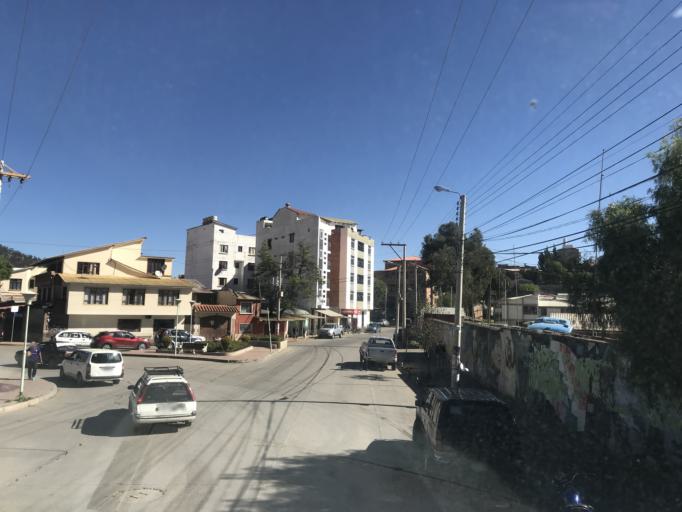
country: BO
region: Chuquisaca
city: Sucre
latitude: -19.0406
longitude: -65.2446
